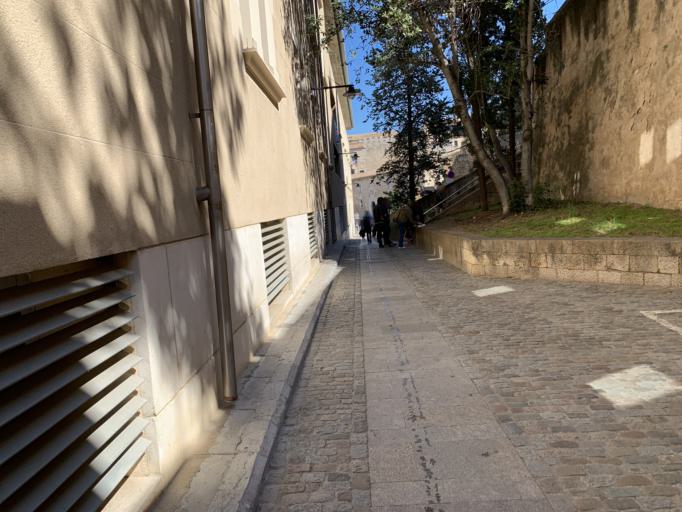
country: ES
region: Catalonia
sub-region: Provincia de Girona
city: Girona
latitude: 41.9850
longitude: 2.8277
